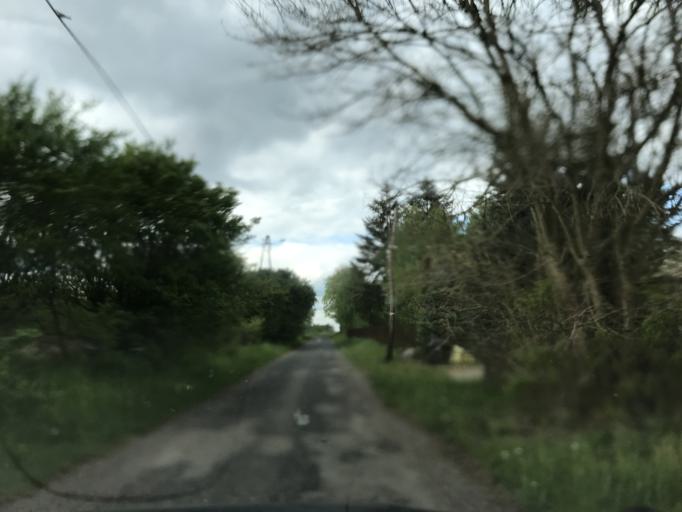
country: PL
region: West Pomeranian Voivodeship
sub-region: Powiat mysliborski
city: Mysliborz
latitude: 52.8878
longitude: 14.8971
